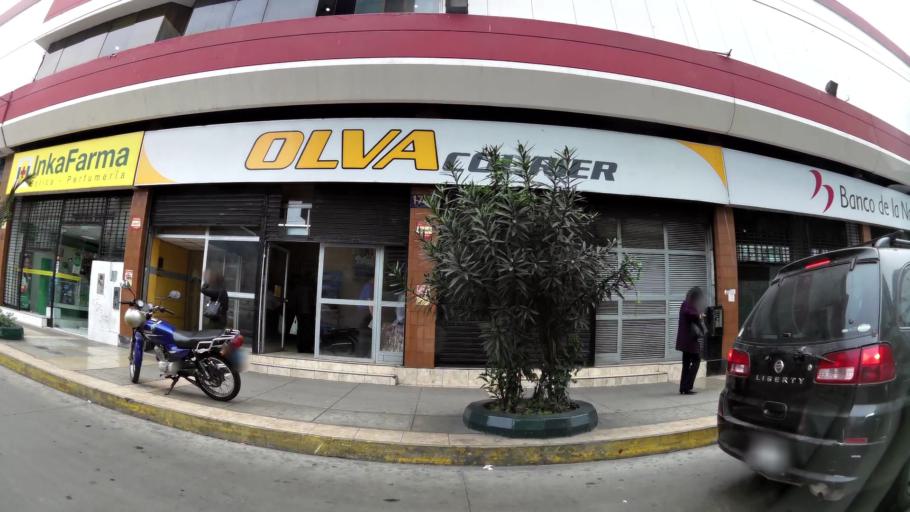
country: PE
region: Lima
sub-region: Lima
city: San Isidro
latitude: -12.0823
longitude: -77.0360
